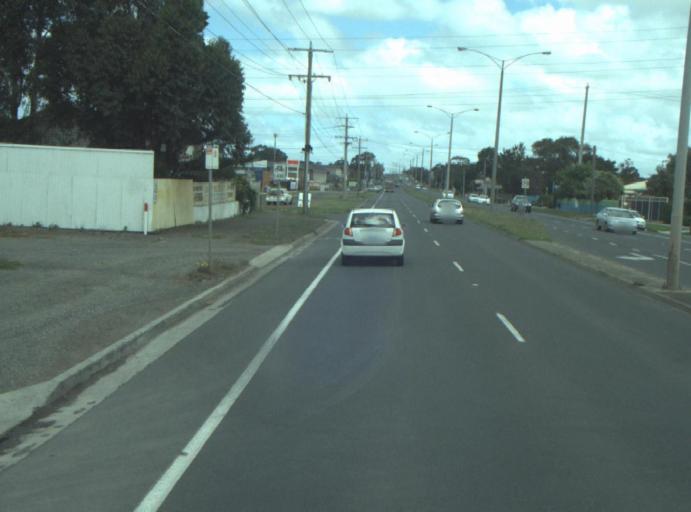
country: AU
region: Victoria
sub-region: Greater Geelong
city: Breakwater
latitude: -38.1969
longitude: 144.3422
